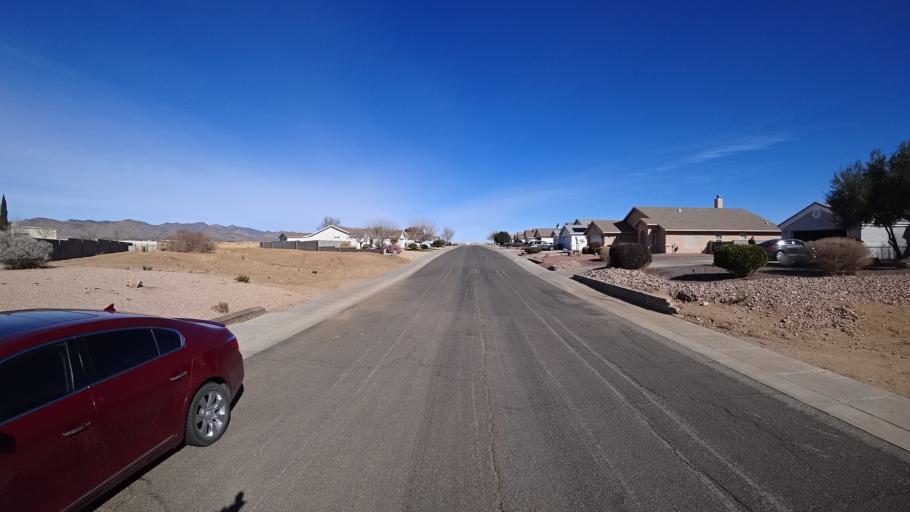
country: US
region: Arizona
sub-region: Mohave County
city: New Kingman-Butler
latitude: 35.2704
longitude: -114.0255
